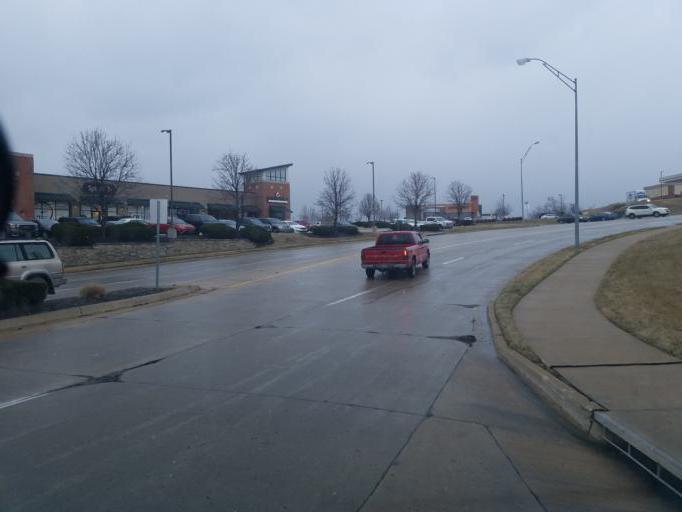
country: US
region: Missouri
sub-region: Boone County
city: Columbia
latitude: 38.9471
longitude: -92.2994
